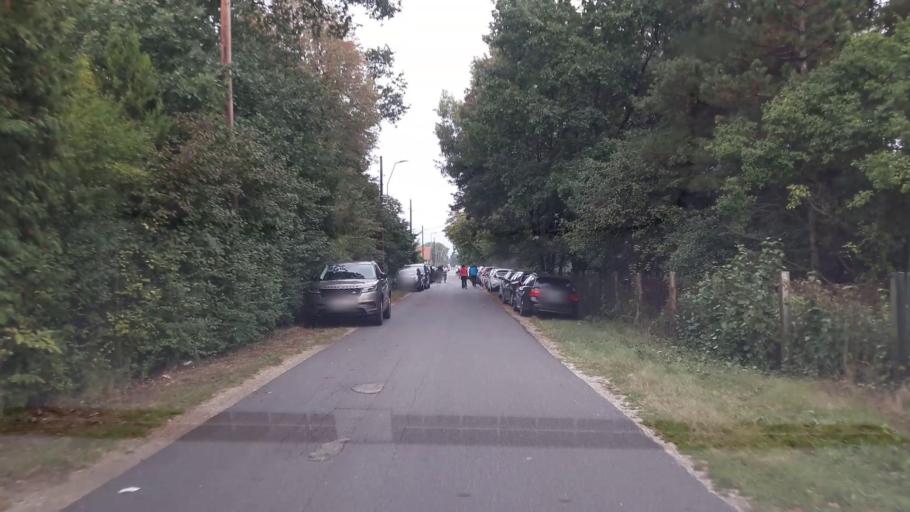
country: AT
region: Lower Austria
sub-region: Politischer Bezirk Ganserndorf
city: Strasshof an der Nordbahn
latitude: 48.3251
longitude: 16.6717
